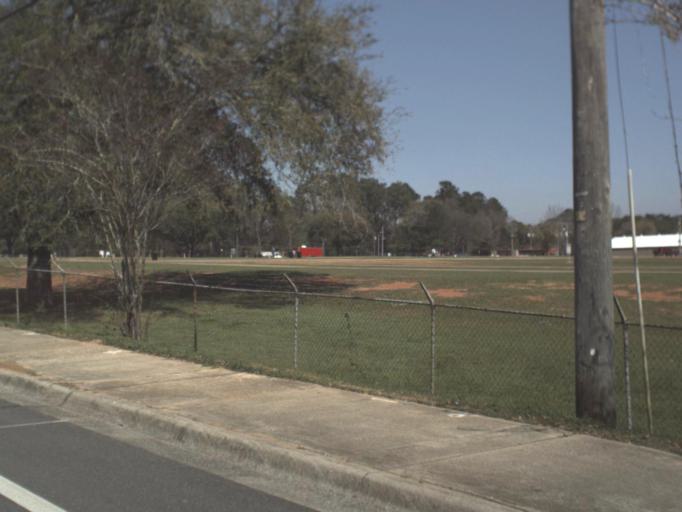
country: US
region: Florida
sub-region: Leon County
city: Tallahassee
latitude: 30.4032
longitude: -84.2805
